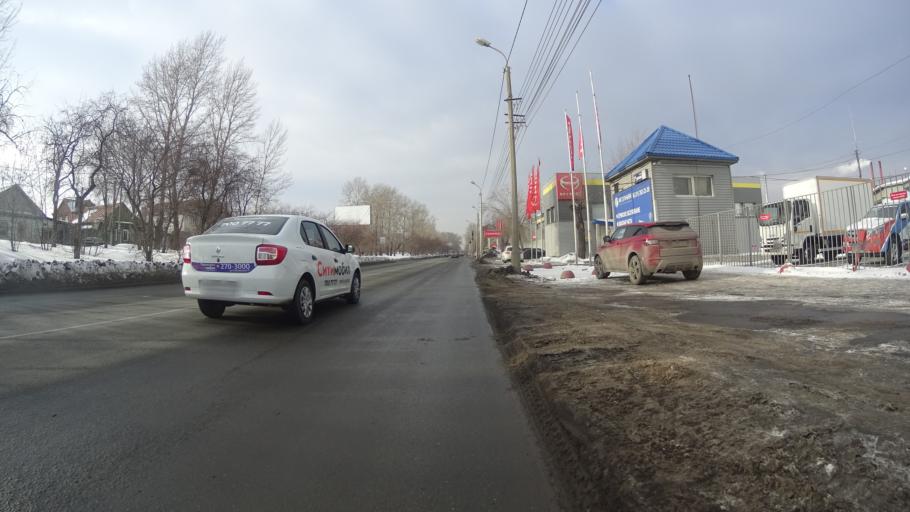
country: RU
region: Chelyabinsk
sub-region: Gorod Chelyabinsk
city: Chelyabinsk
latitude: 55.1193
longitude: 61.3823
